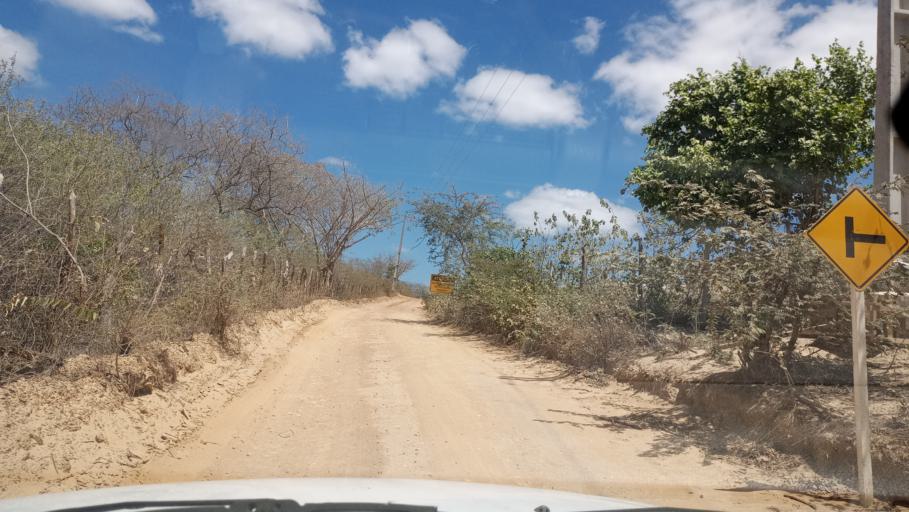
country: BR
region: Rio Grande do Norte
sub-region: Sao Paulo Do Potengi
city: Sao Paulo do Potengi
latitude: -5.7911
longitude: -35.9189
